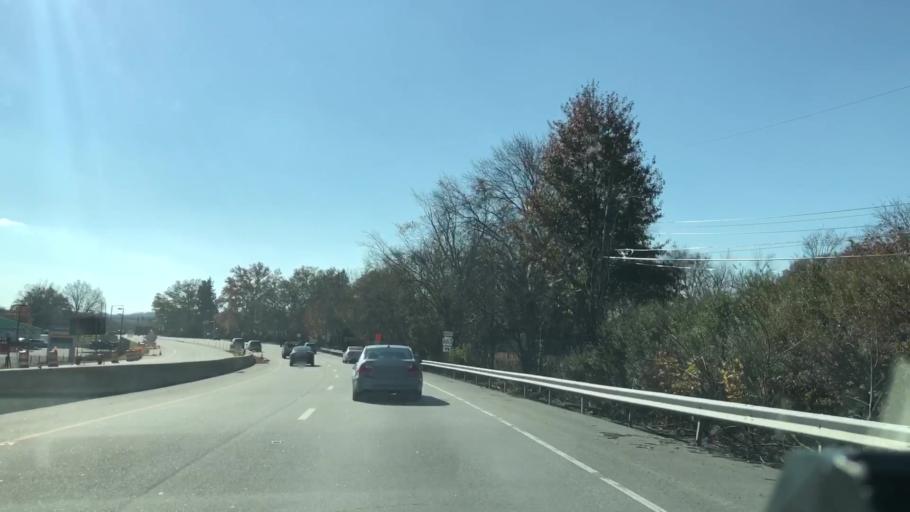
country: US
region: Pennsylvania
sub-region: Montgomery County
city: Pottstown
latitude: 40.2515
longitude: -75.6613
